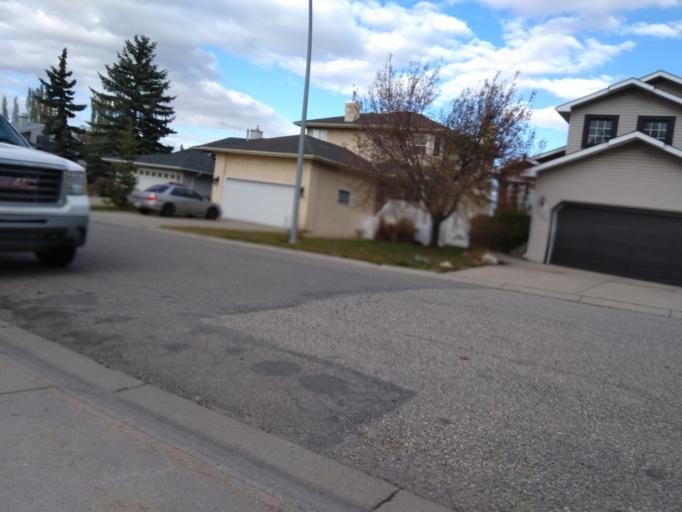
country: CA
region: Alberta
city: Calgary
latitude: 51.1399
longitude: -114.1183
